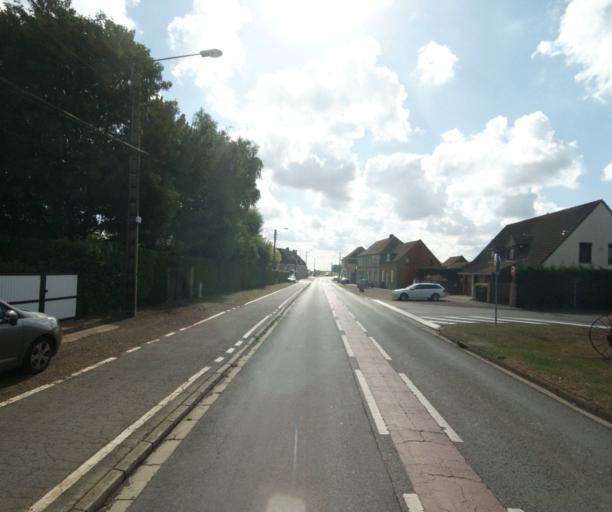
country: FR
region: Nord-Pas-de-Calais
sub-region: Departement du Nord
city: Sailly-lez-Lannoy
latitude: 50.6484
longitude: 3.2263
